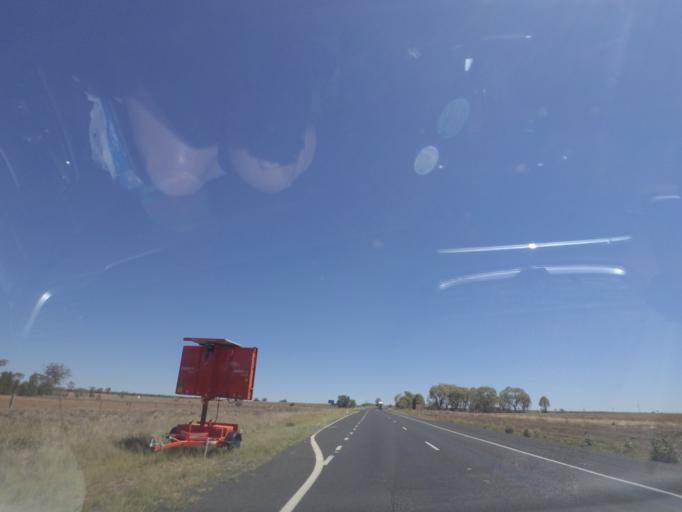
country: AU
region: New South Wales
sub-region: Gilgandra
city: Gilgandra
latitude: -31.6691
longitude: 148.7167
